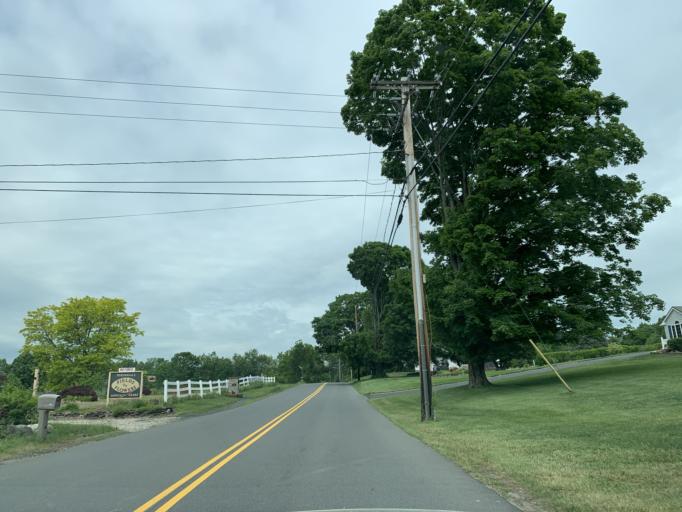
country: US
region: Massachusetts
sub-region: Hampshire County
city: Southampton
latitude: 42.1852
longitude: -72.7411
